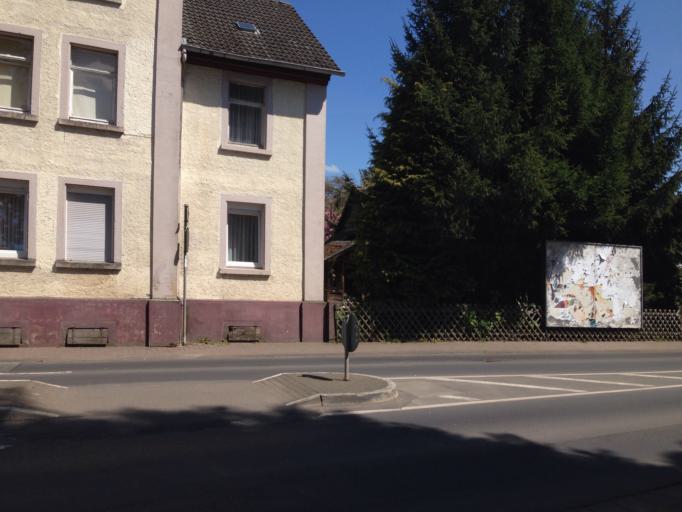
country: DE
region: Hesse
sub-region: Regierungsbezirk Giessen
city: Laubach
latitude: 50.5412
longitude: 8.9874
